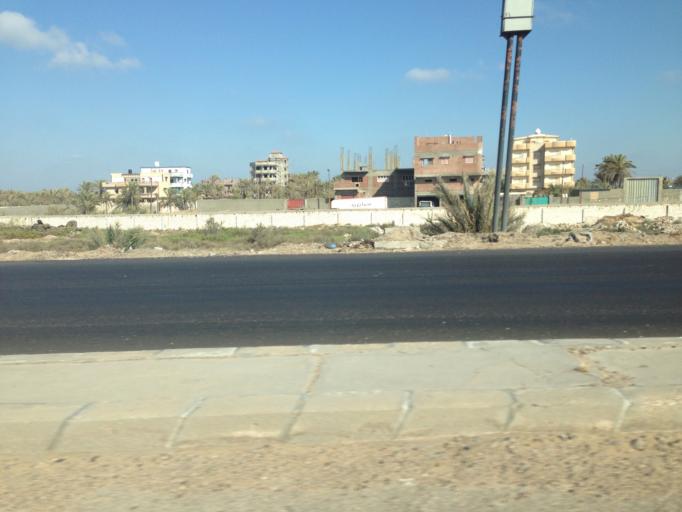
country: EG
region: Al Buhayrah
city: Idku
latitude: 31.3073
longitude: 30.2743
